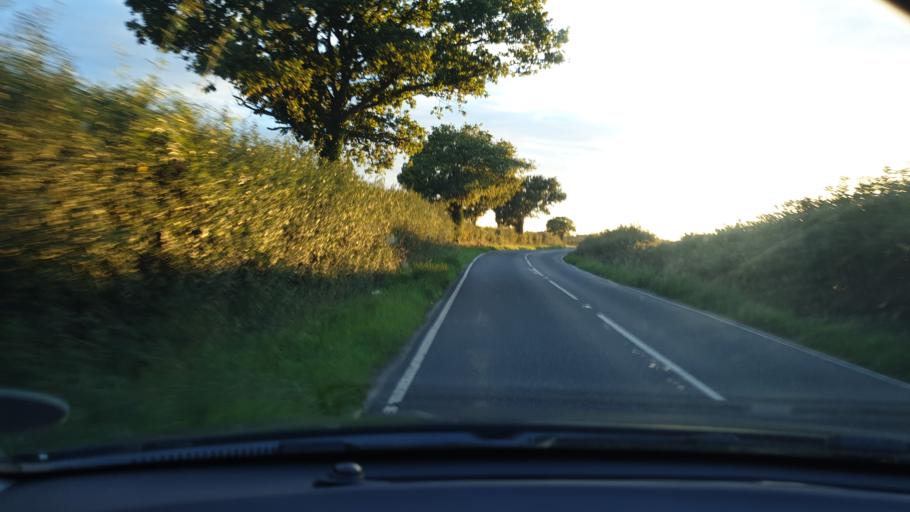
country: GB
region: England
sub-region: Essex
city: Alresford
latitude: 51.9052
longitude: 0.9834
